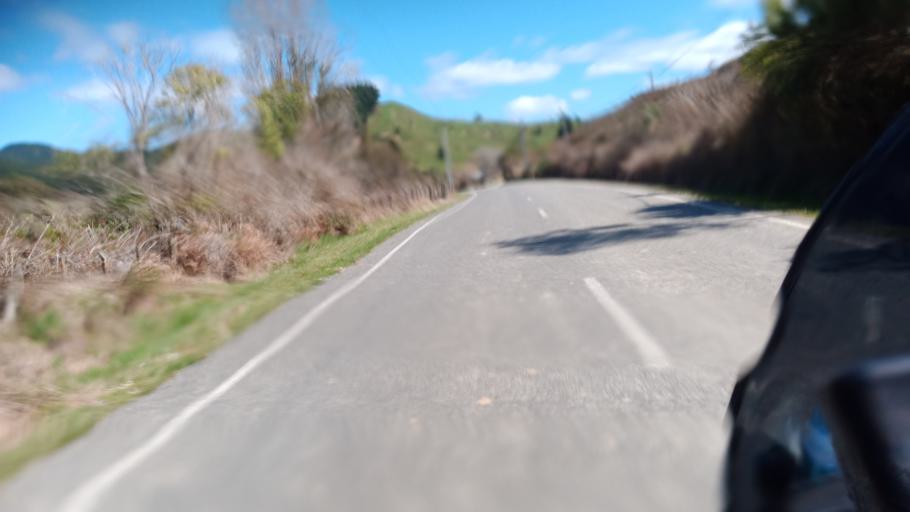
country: NZ
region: Gisborne
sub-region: Gisborne District
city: Gisborne
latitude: -38.7869
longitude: 177.7978
